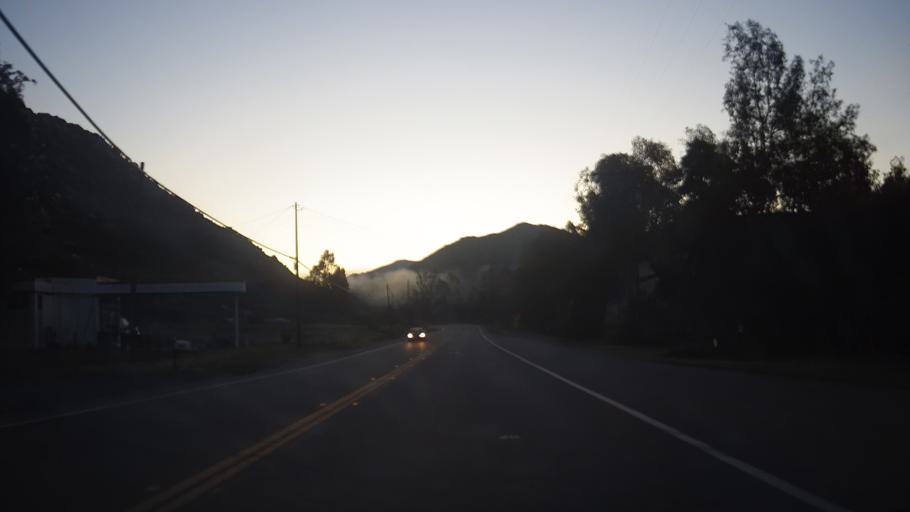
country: US
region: California
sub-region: San Diego County
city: Crest
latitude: 32.7801
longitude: -116.8719
